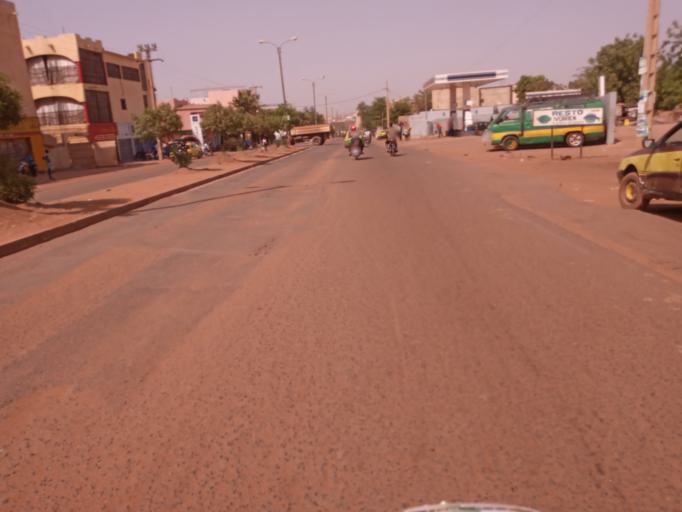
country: ML
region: Bamako
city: Bamako
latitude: 12.5780
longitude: -7.9485
